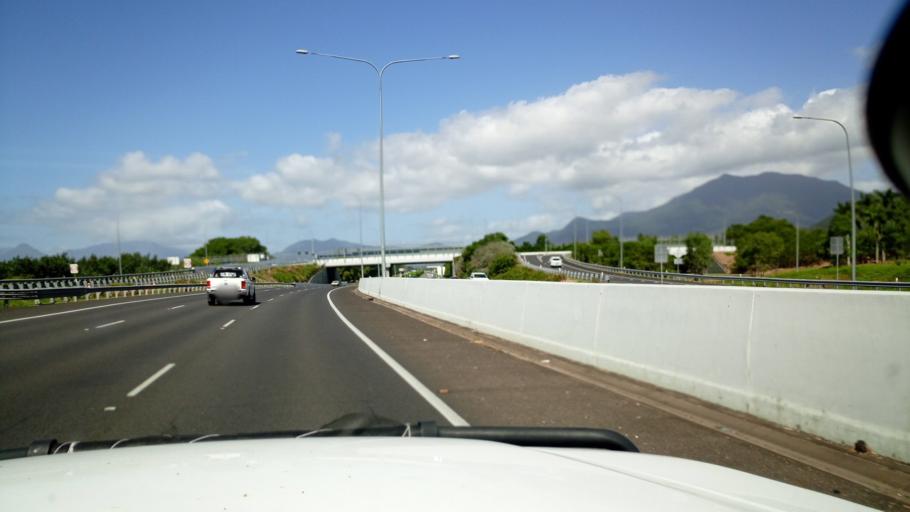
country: AU
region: Queensland
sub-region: Cairns
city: Woree
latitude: -16.9749
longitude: 145.7440
